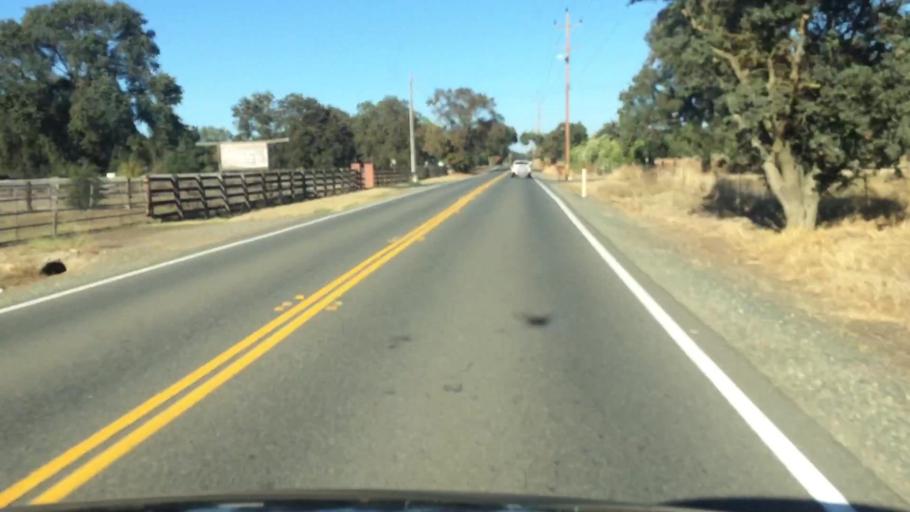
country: US
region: California
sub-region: Sacramento County
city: Wilton
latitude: 38.4321
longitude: -121.2011
